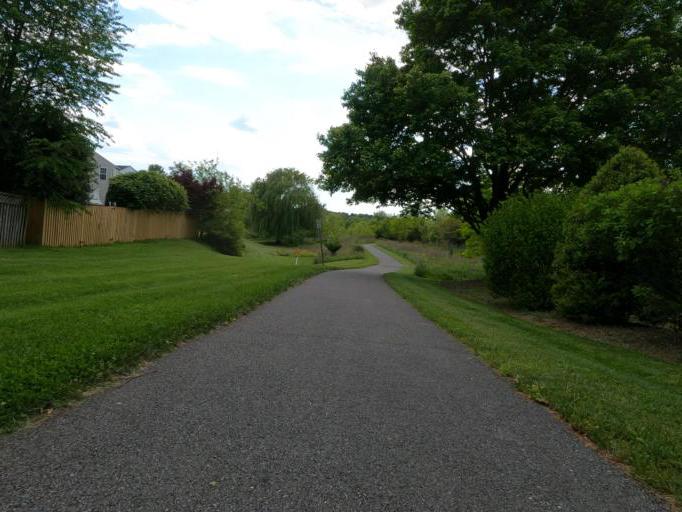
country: US
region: Maryland
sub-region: Montgomery County
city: Clarksburg
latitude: 39.2094
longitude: -77.2538
